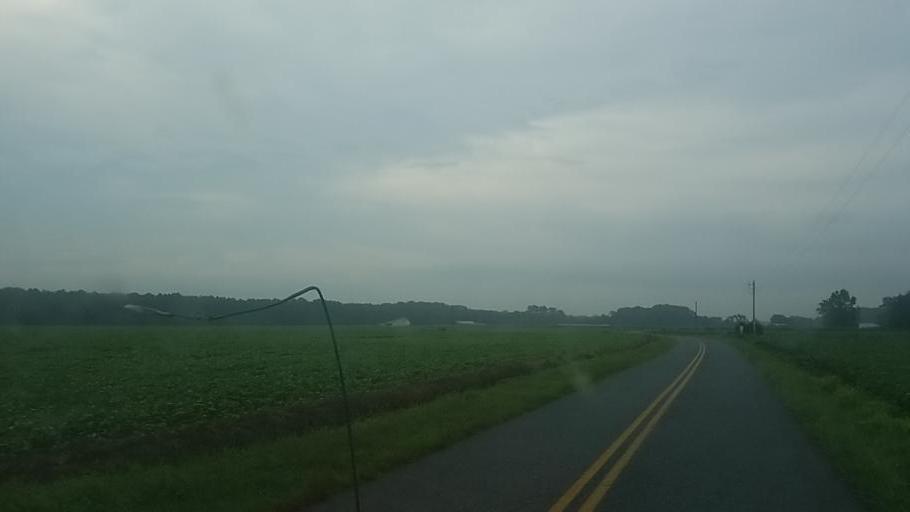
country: US
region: Maryland
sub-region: Wicomico County
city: Pittsville
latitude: 38.4254
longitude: -75.3206
